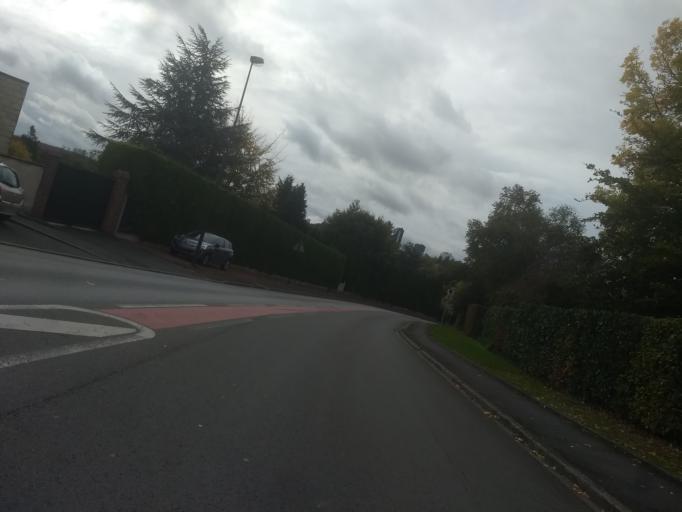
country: FR
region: Nord-Pas-de-Calais
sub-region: Departement du Pas-de-Calais
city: Anzin-Saint-Aubin
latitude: 50.3101
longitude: 2.7506
